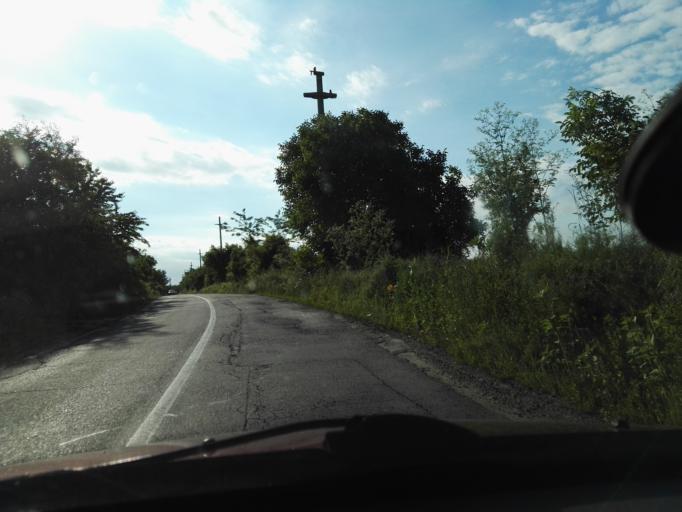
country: RO
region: Ilfov
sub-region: Comuna Copaceni
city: Copaceni
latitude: 44.2353
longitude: 26.1223
